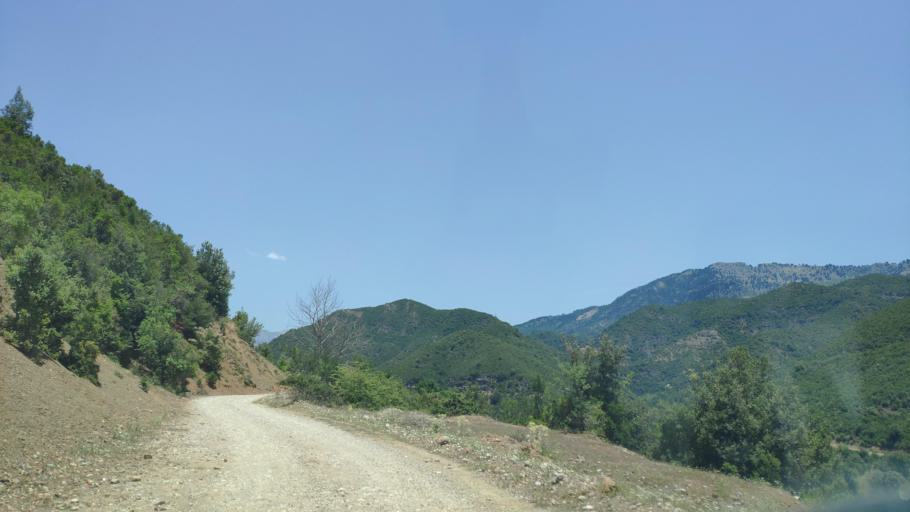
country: GR
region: Thessaly
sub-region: Nomos Kardhitsas
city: Anthiro
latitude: 39.1748
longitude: 21.3702
